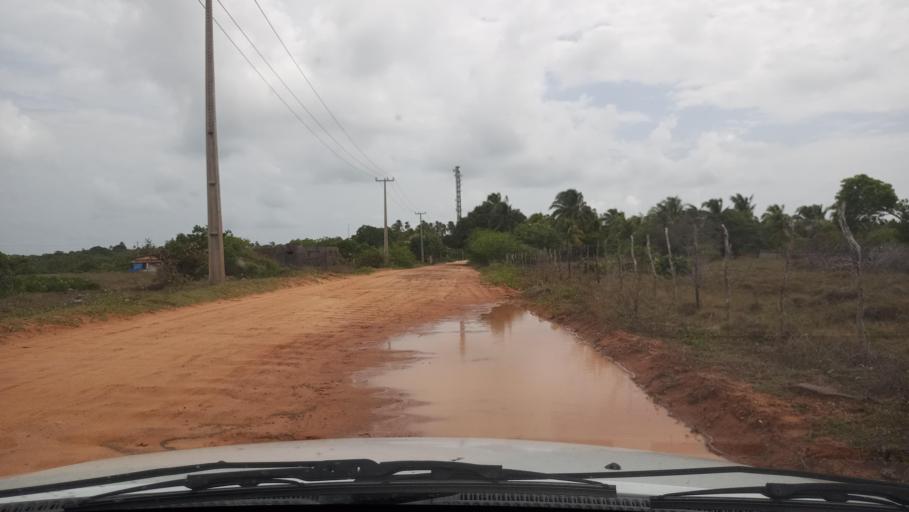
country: BR
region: Rio Grande do Norte
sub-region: Maxaranguape
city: Sao Miguel
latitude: -5.4653
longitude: -35.2962
